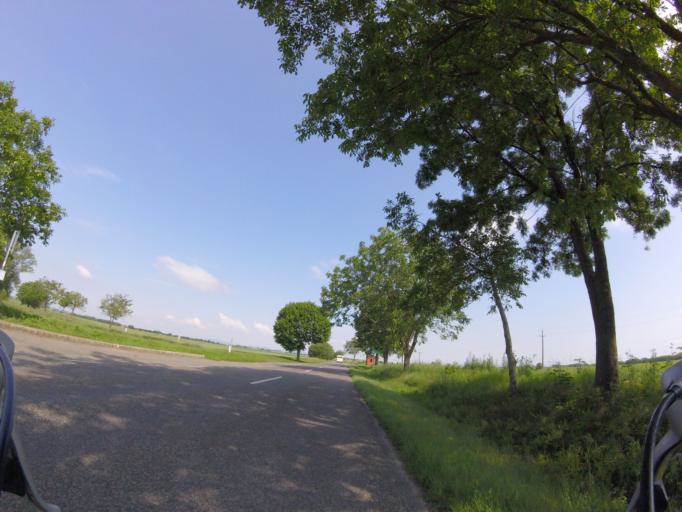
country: HU
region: Baranya
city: Kozarmisleny
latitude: 45.9718
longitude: 18.3428
